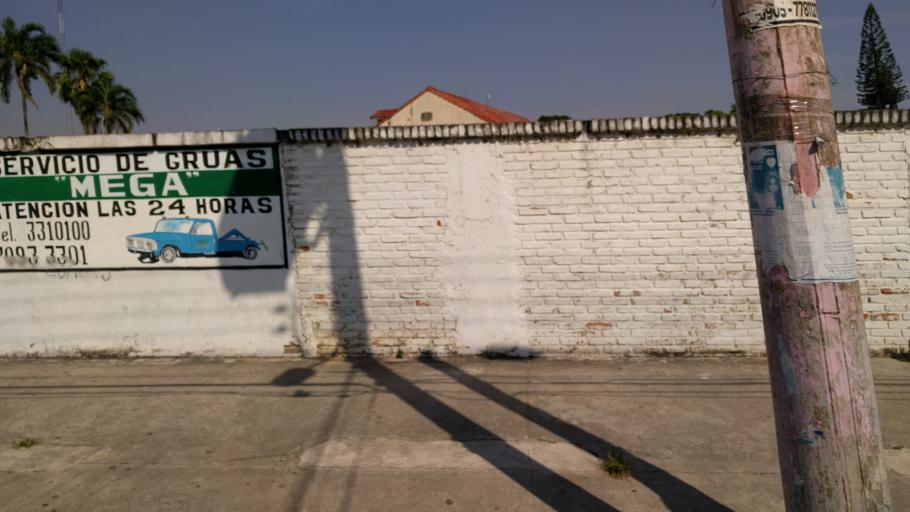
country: BO
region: Santa Cruz
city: Santa Cruz de la Sierra
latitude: -17.8138
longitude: -63.1814
